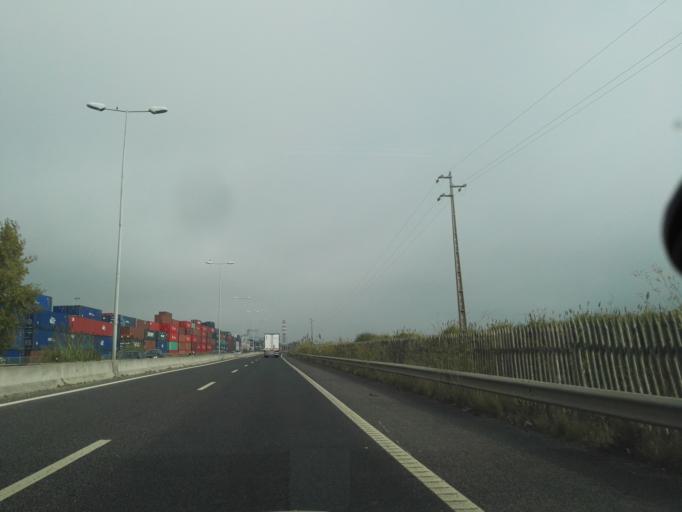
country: PT
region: Lisbon
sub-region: Loures
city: Sao Joao da Talha
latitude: 38.8164
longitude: -9.0873
